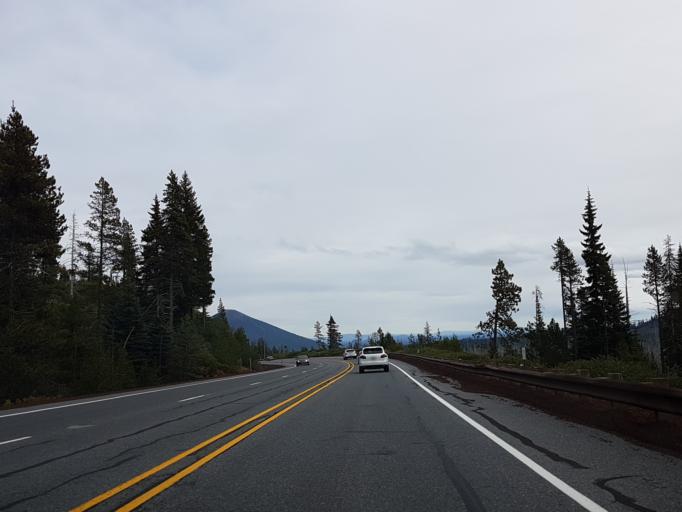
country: US
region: Oregon
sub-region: Deschutes County
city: Sisters
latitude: 44.4250
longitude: -121.8177
